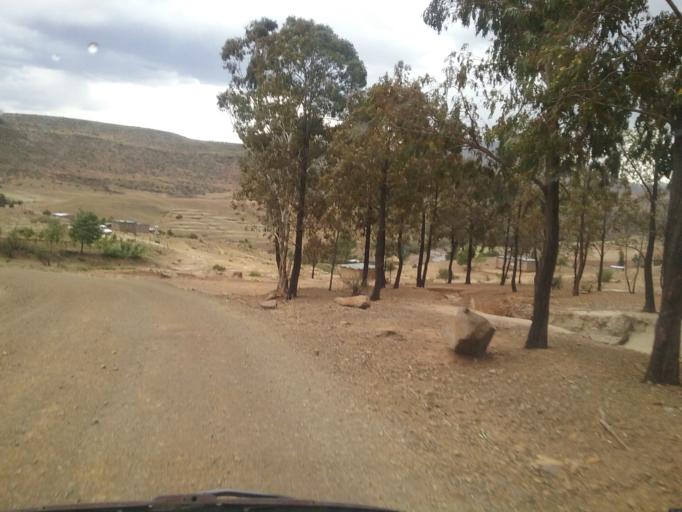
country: LS
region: Quthing
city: Quthing
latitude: -30.3003
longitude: 27.8143
